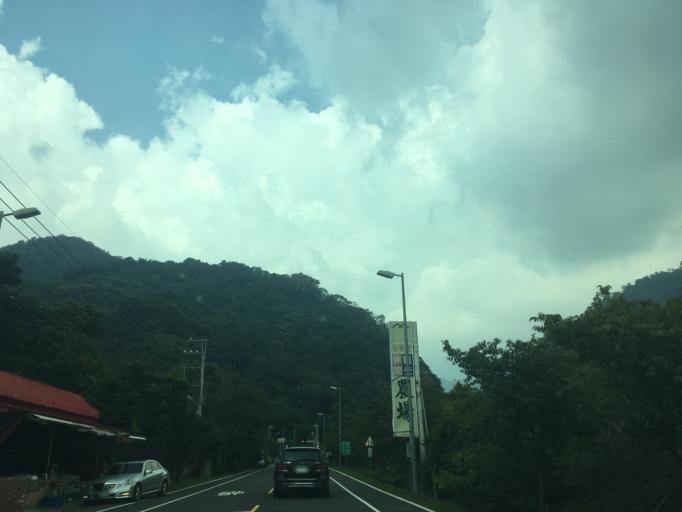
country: TW
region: Taiwan
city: Fengyuan
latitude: 24.2943
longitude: 120.9061
